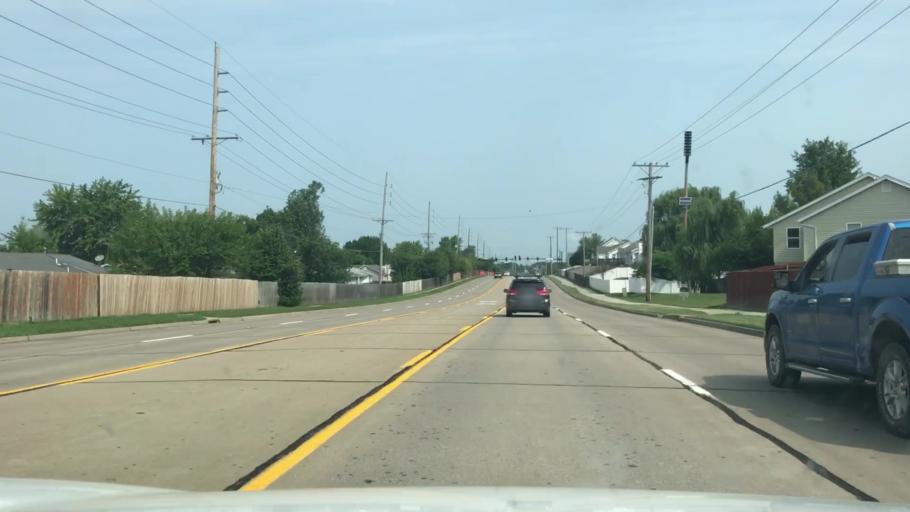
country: US
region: Missouri
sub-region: Saint Charles County
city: Dardenne Prairie
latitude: 38.7818
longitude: -90.7372
